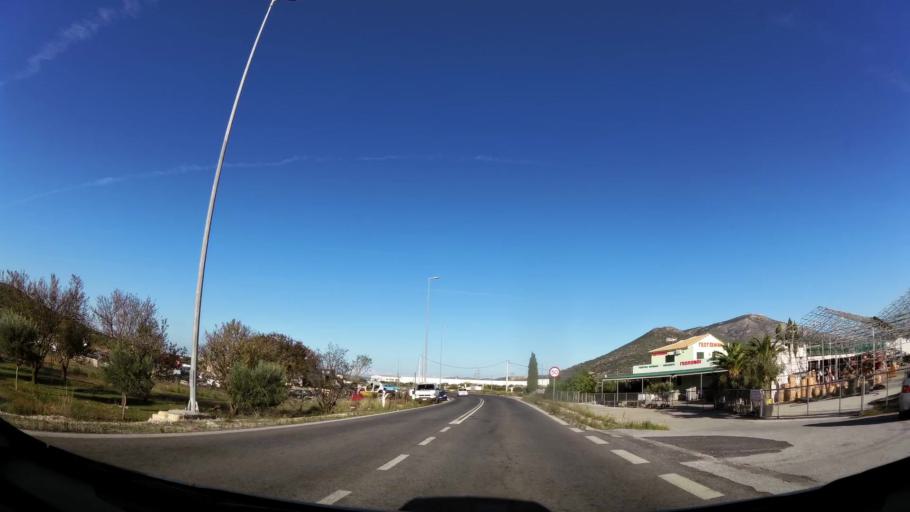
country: GR
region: Attica
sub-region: Nomarchia Anatolikis Attikis
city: Kalyvia Thorikou
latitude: 37.8513
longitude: 23.9166
